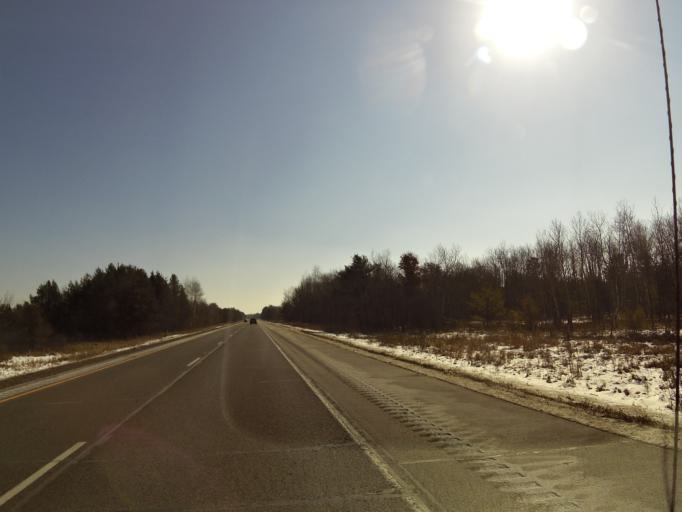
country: US
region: Wisconsin
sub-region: Jackson County
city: Black River Falls
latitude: 44.2566
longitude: -90.7631
